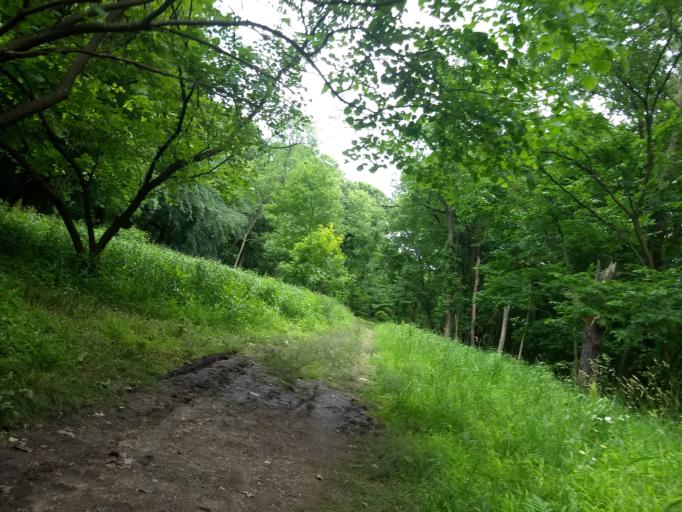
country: US
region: Pennsylvania
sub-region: Allegheny County
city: Wilkinsburg
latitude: 40.4368
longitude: -79.9053
